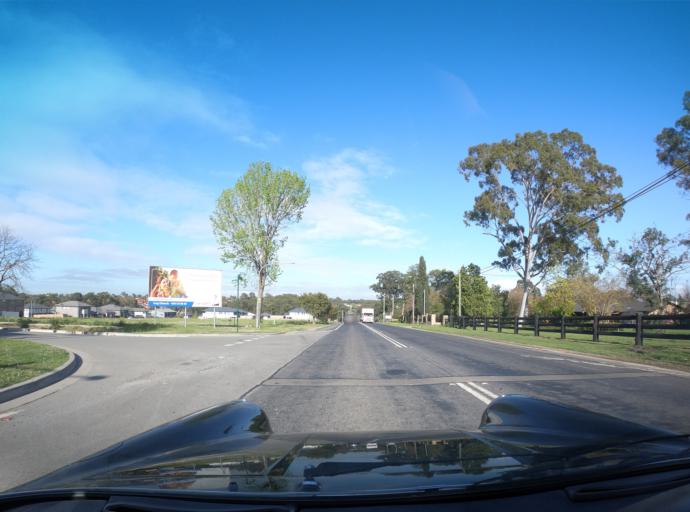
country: AU
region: New South Wales
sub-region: The Hills Shire
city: Beaumont Hills
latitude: -33.6868
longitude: 150.9474
